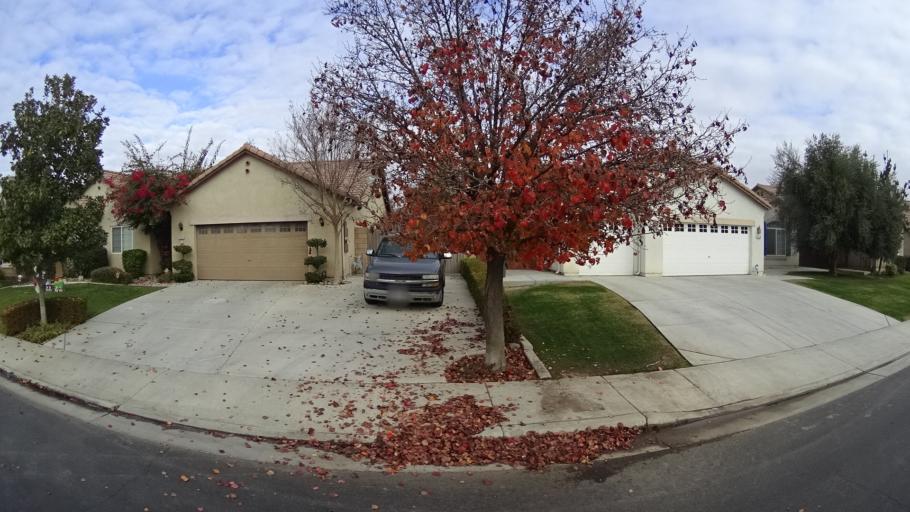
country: US
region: California
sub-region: Kern County
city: Rosedale
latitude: 35.2994
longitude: -119.1297
